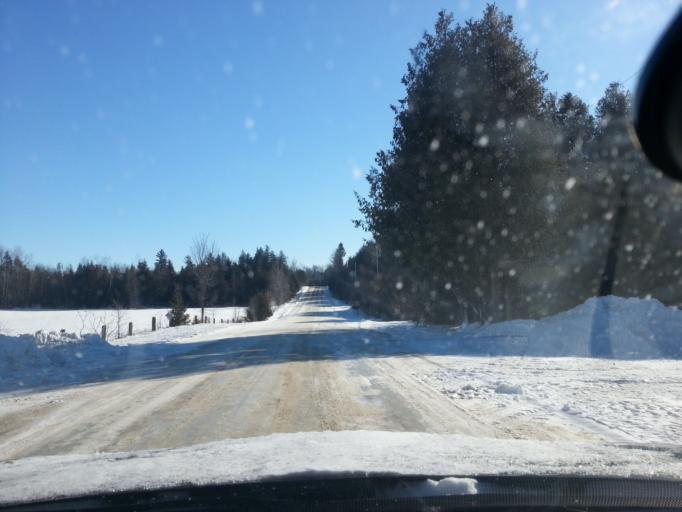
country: CA
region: Ontario
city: Arnprior
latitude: 45.2506
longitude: -76.3117
